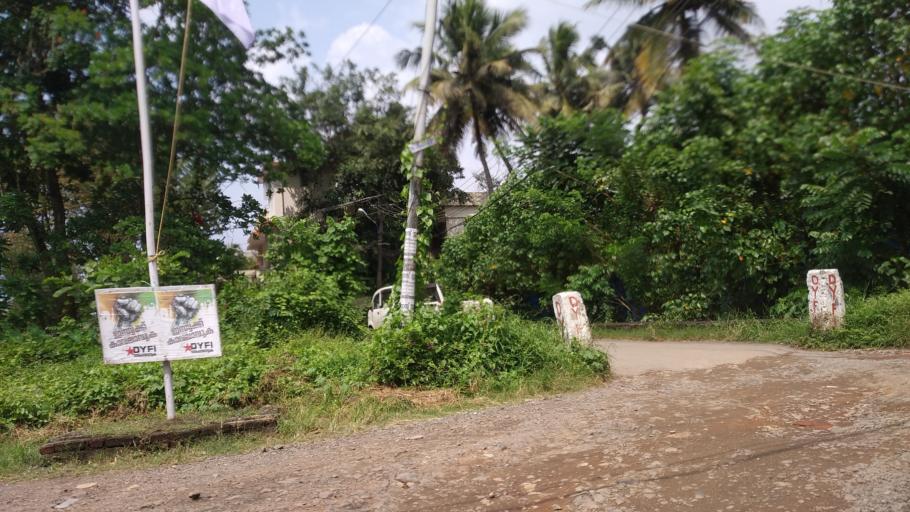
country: IN
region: Kerala
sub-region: Ernakulam
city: Cochin
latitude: 9.9697
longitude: 76.3022
